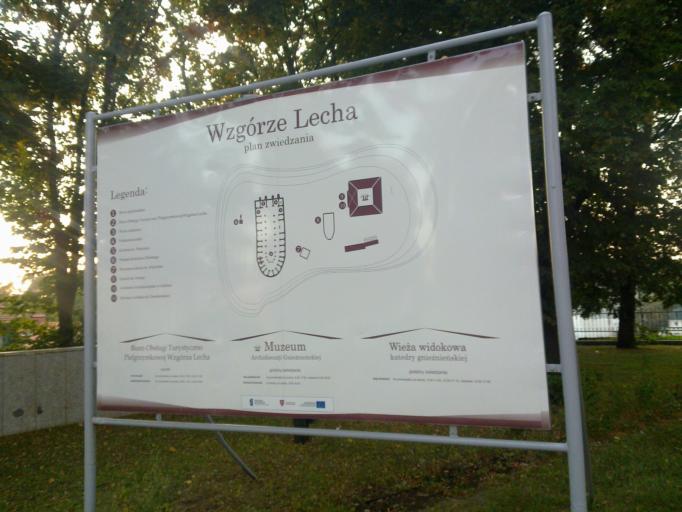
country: PL
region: Greater Poland Voivodeship
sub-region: Powiat gnieznienski
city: Gniezno
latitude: 52.5368
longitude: 17.5919
